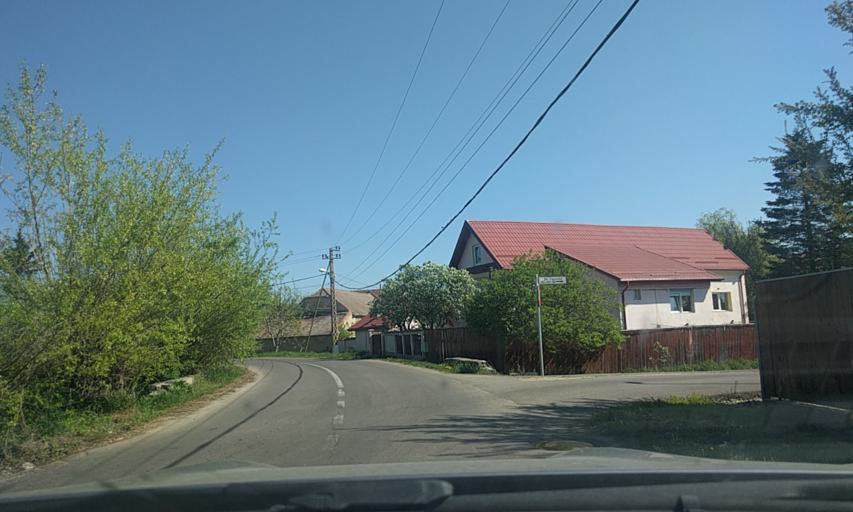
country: RO
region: Brasov
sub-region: Comuna Bod
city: Colonia Bod
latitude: 45.7092
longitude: 25.5700
